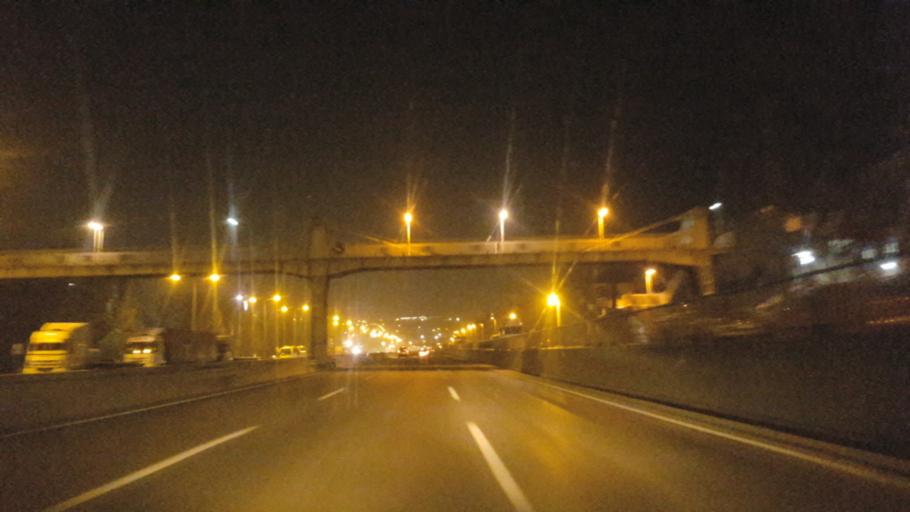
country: TR
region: Kocaeli
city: Tavsancil
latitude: 40.7830
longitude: 29.5378
